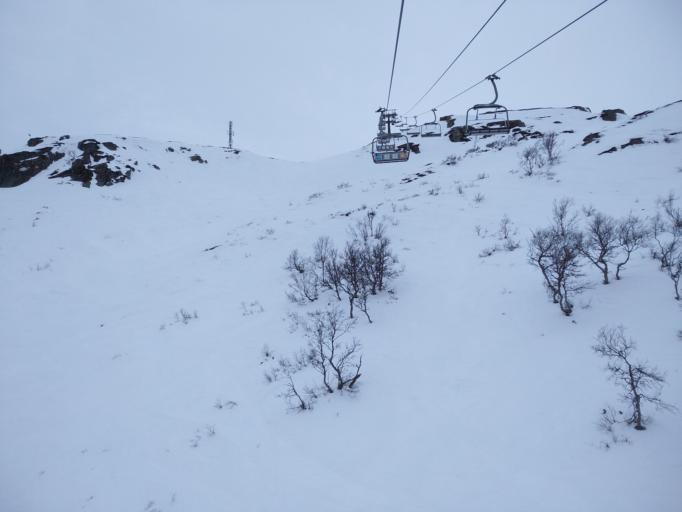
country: NO
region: Aust-Agder
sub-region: Bykle
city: Hovden
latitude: 59.5770
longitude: 7.3364
